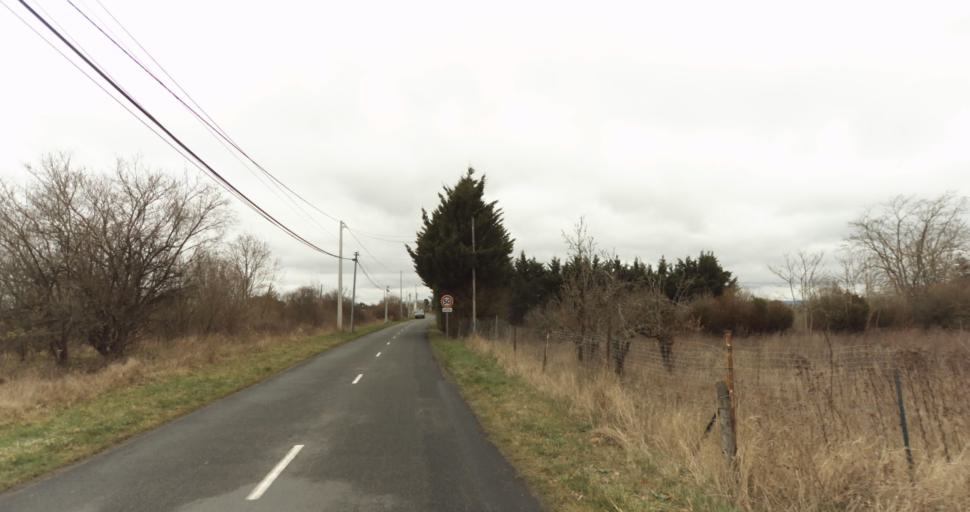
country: FR
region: Pays de la Loire
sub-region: Departement de Maine-et-Loire
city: Distre
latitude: 47.2401
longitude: -0.1049
